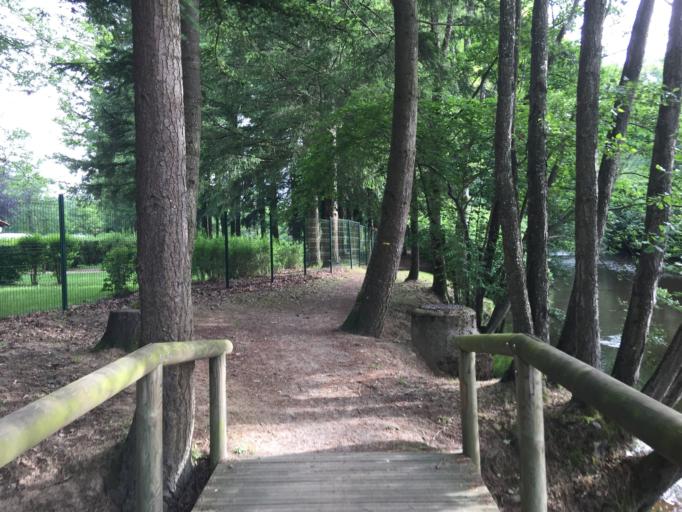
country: FR
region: Auvergne
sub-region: Departement du Puy-de-Dome
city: Ambert
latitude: 45.5397
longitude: 3.7302
